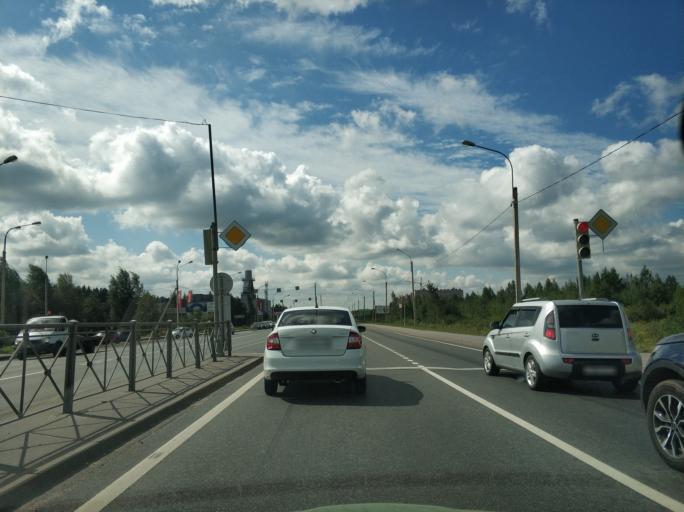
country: RU
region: Leningrad
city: Vsevolozhsk
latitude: 60.0273
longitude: 30.6172
